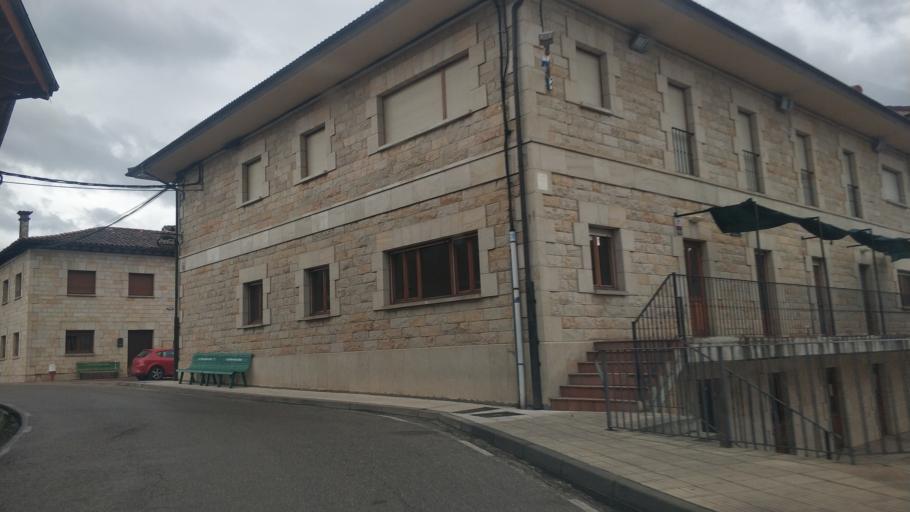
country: ES
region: Castille and Leon
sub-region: Provincia de Burgos
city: Canicosa de la Sierra
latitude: 41.9359
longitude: -3.0420
